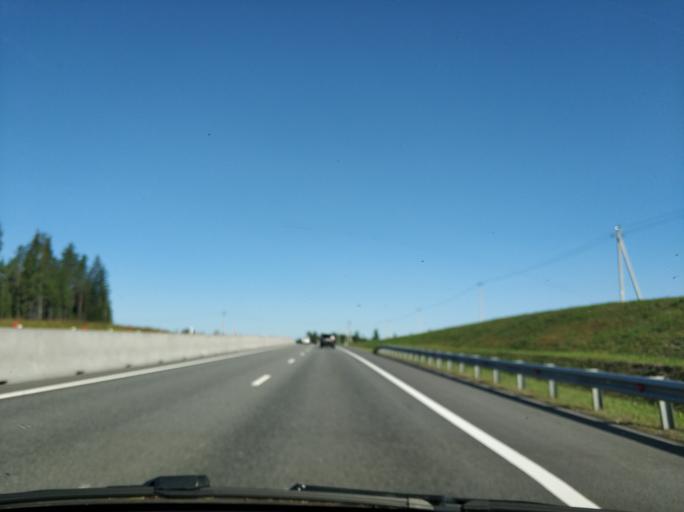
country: RU
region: Leningrad
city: Sosnovo
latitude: 60.5128
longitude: 30.1864
